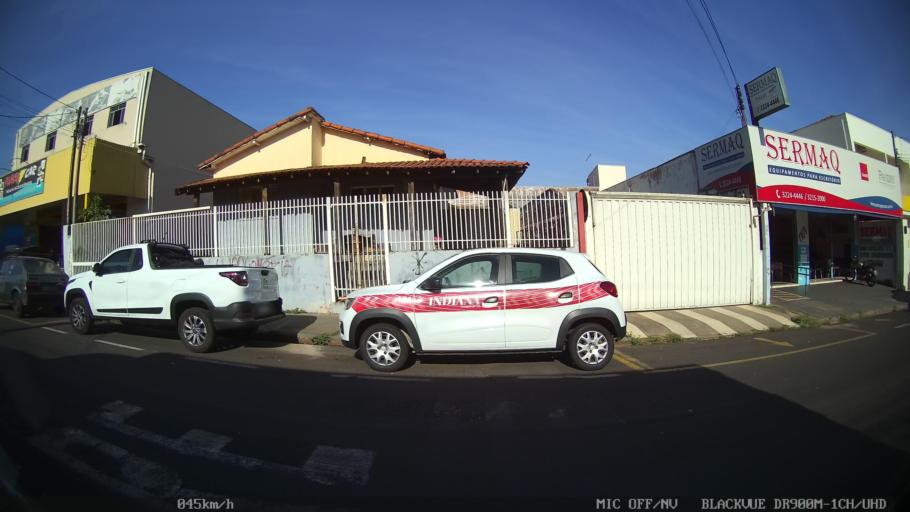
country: BR
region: Sao Paulo
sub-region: Sao Jose Do Rio Preto
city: Sao Jose do Rio Preto
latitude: -20.7966
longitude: -49.3651
